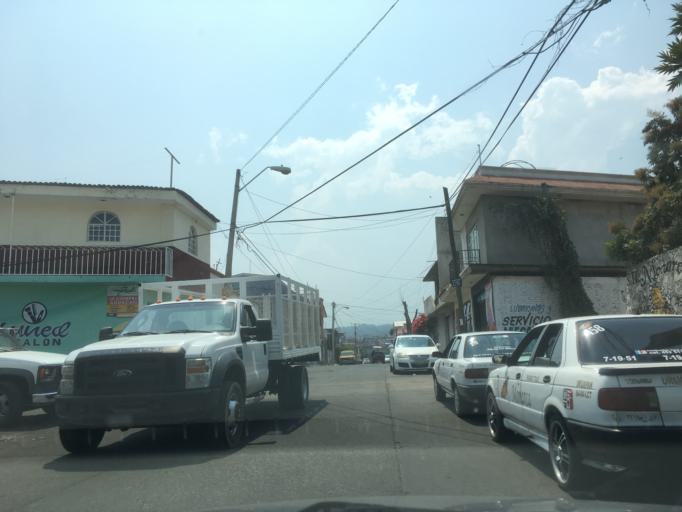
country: MX
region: Michoacan
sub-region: Uruapan
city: Uruapan
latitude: 19.4128
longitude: -102.0692
